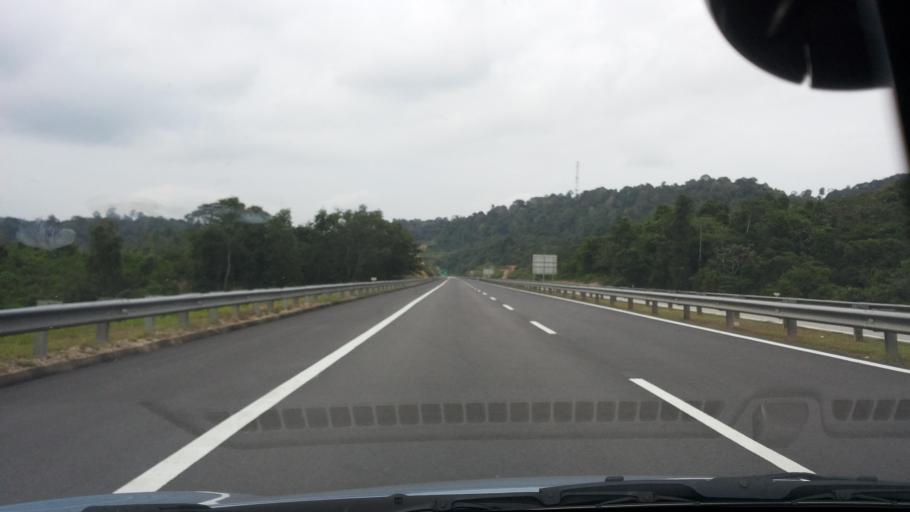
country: MY
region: Pahang
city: Kuantan
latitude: 3.7491
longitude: 103.1232
